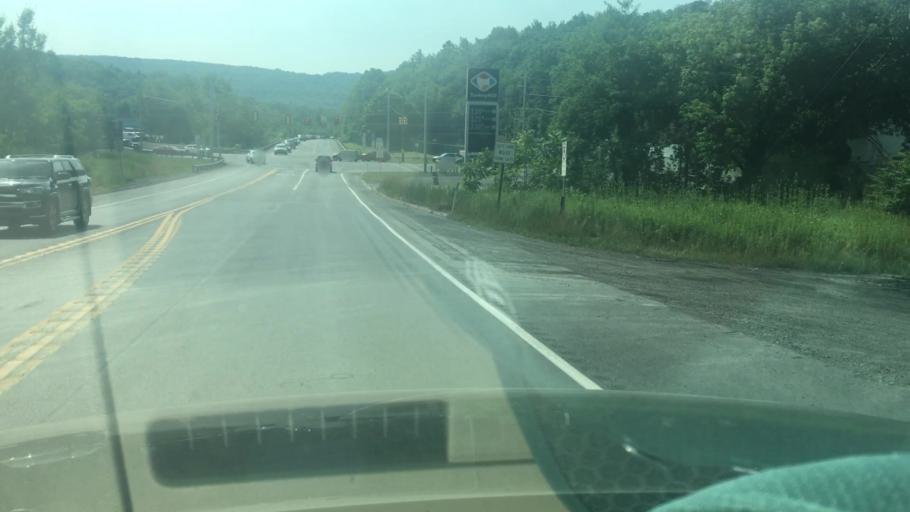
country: US
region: Pennsylvania
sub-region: Northumberland County
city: Mount Carmel
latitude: 40.7997
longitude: -76.4382
